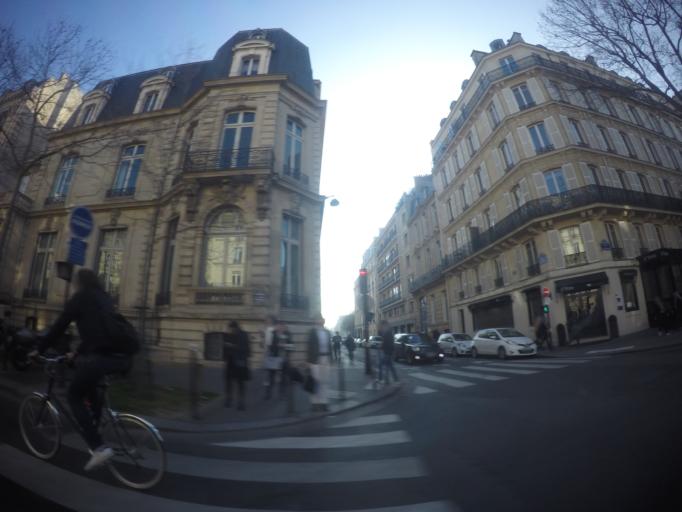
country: FR
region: Ile-de-France
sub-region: Departement des Hauts-de-Seine
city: Clichy
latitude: 48.8612
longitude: 2.3103
